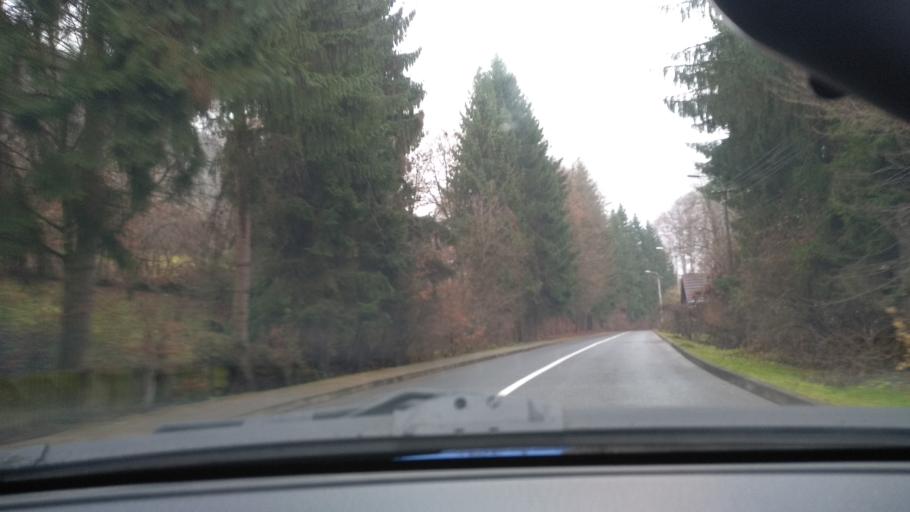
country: RO
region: Mures
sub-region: Oras Sovata
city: Sovata
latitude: 46.5958
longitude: 25.0813
